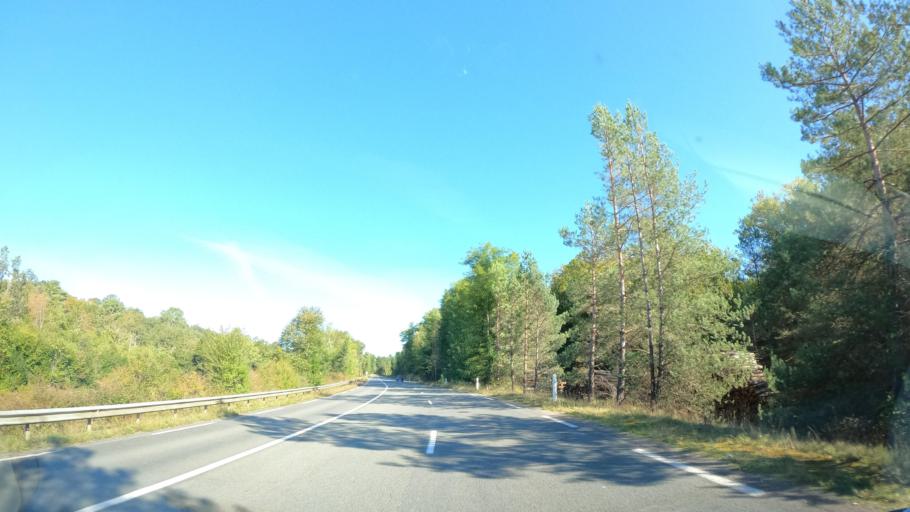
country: FR
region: Aquitaine
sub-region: Departement de la Dordogne
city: Vergt
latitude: 45.0583
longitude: 0.6779
